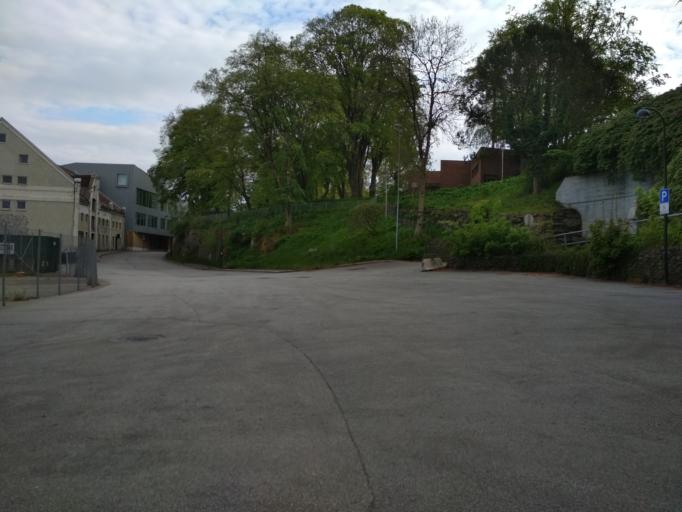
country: NO
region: Rogaland
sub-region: Stavanger
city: Stavanger
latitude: 58.9779
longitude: 5.7209
